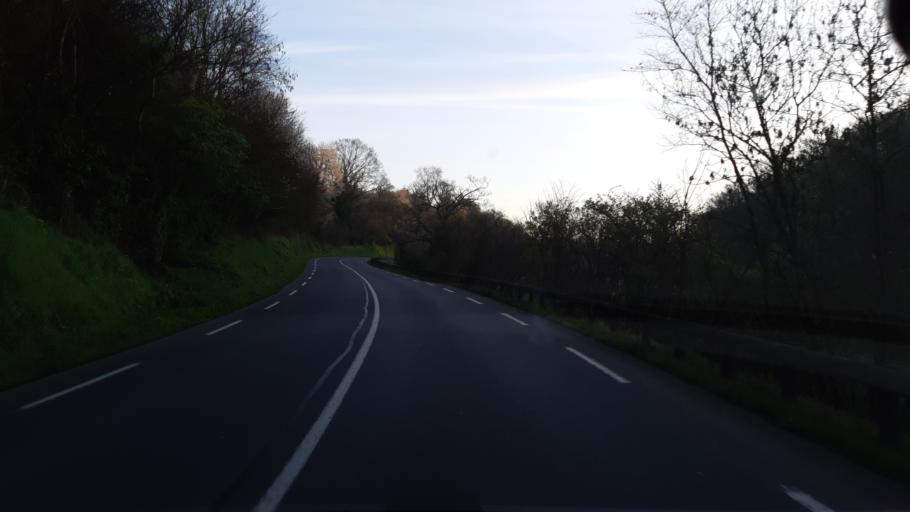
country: FR
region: Lower Normandy
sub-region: Departement de la Manche
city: Agneaux
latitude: 49.0732
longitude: -1.1277
